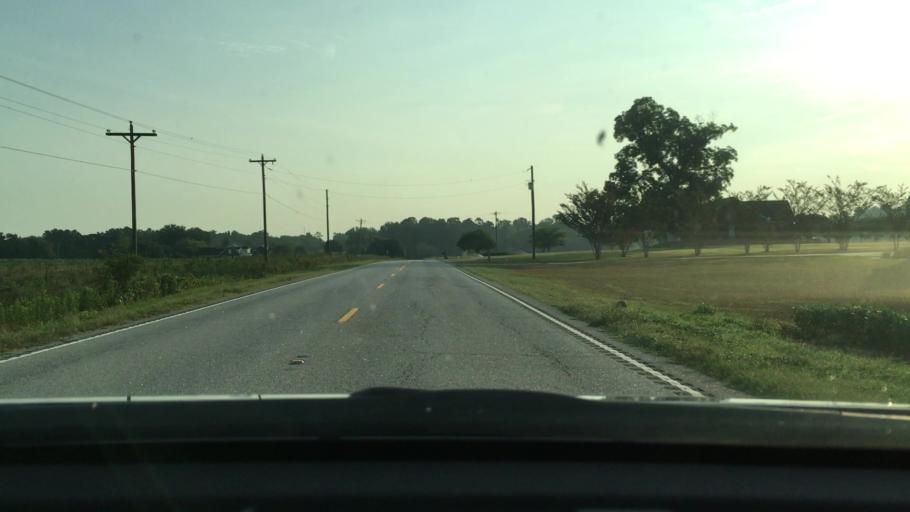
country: US
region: South Carolina
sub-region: Florence County
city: Timmonsville
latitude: 34.1858
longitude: -80.0474
